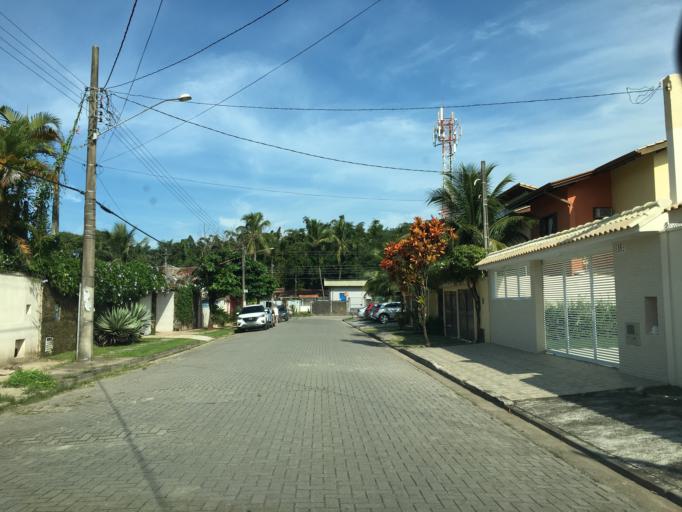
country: BR
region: Sao Paulo
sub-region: Sao Sebastiao
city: Sao Sebastiao
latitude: -23.7654
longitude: -45.7278
